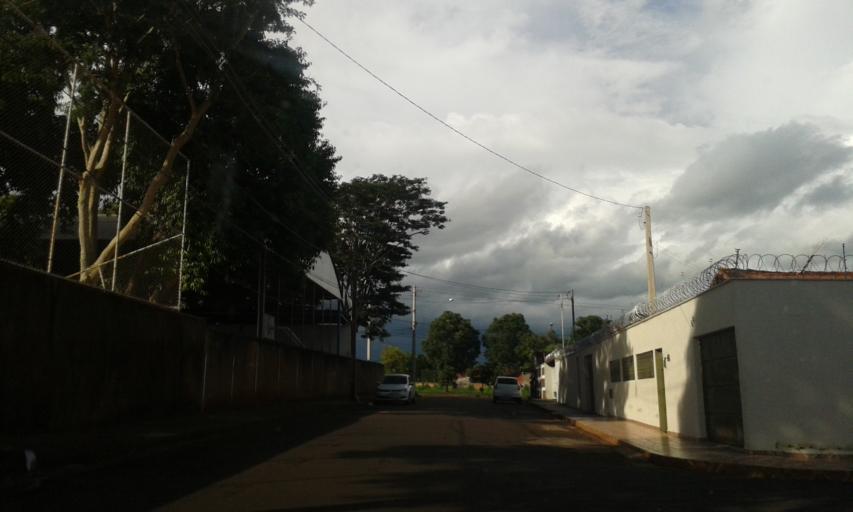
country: BR
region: Minas Gerais
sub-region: Ituiutaba
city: Ituiutaba
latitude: -18.9687
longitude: -49.4511
